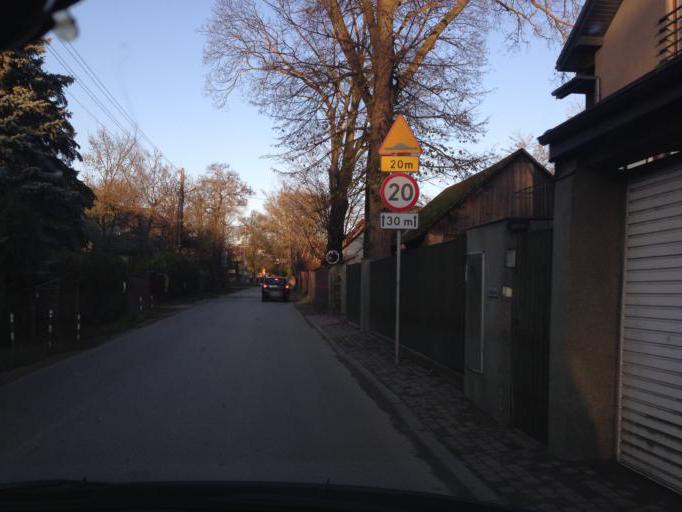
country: PL
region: Lesser Poland Voivodeship
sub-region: Powiat krakowski
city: Rzaska
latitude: 50.0750
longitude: 19.8780
